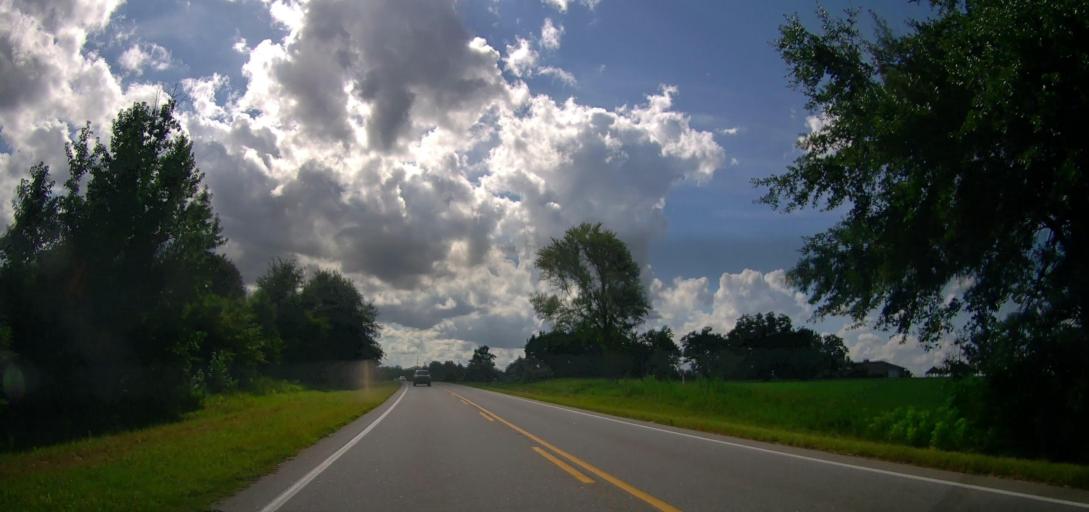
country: US
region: Alabama
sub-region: Russell County
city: Ladonia
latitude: 32.4621
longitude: -85.1558
